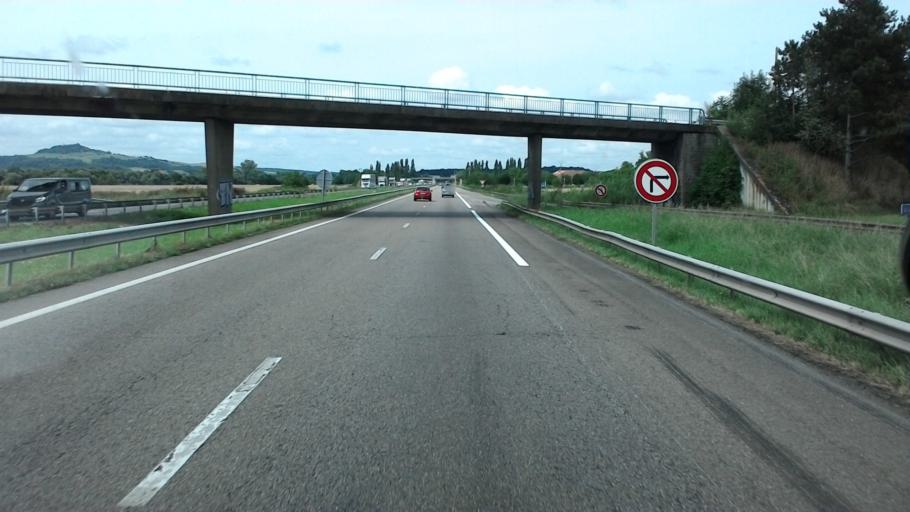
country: FR
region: Lorraine
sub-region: Departement de Meurthe-et-Moselle
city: Dieulouard
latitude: 48.8618
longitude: 6.0915
